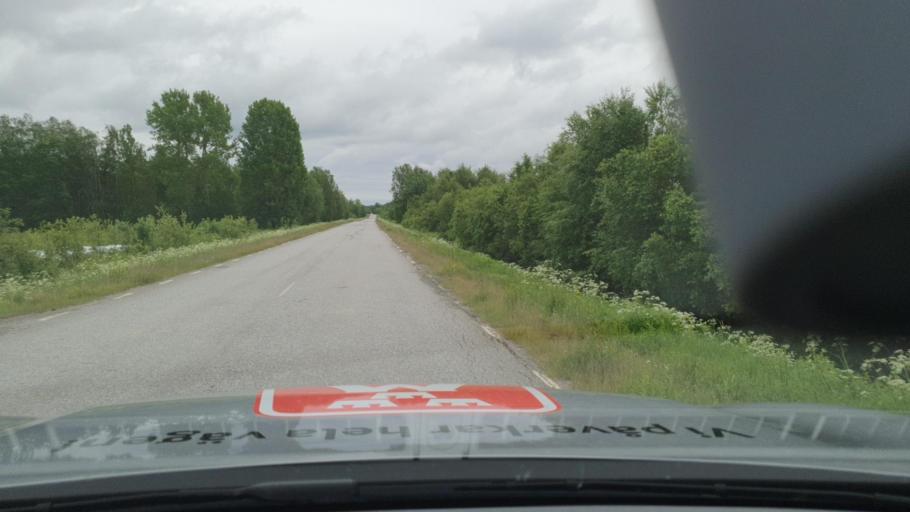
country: SE
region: Norrbotten
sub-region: Lulea Kommun
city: Ranea
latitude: 65.8486
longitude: 22.2485
